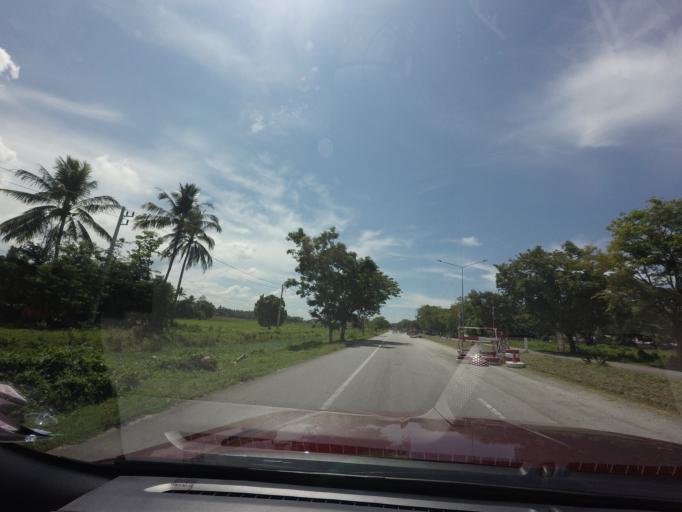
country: TH
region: Pattani
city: Mai Kaen
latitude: 6.5824
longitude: 101.6371
